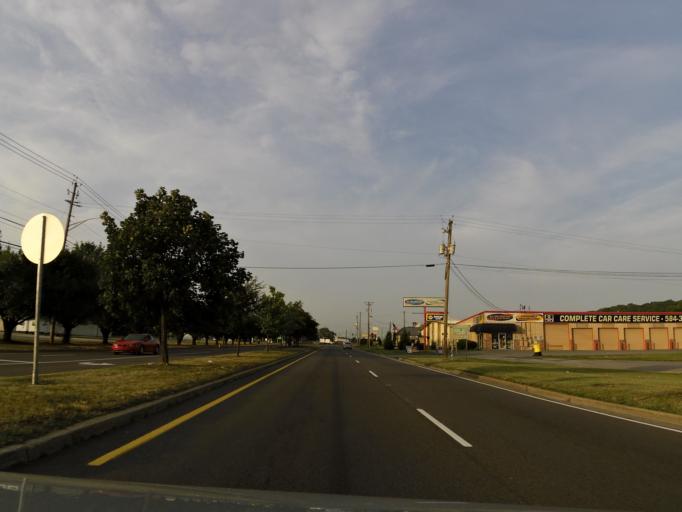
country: US
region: Tennessee
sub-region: Knox County
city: Knoxville
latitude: 35.9549
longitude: -84.0083
